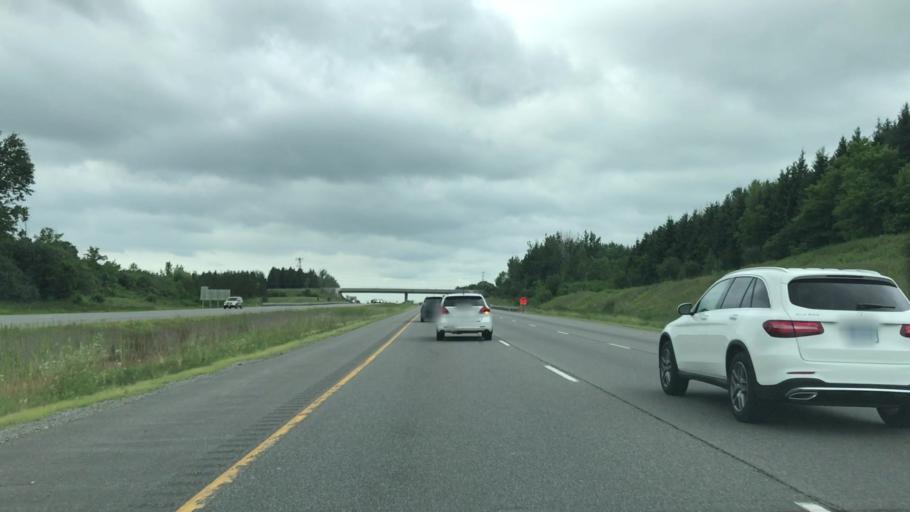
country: CA
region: Ontario
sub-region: York
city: Richmond Hill
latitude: 43.9622
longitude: -79.3930
